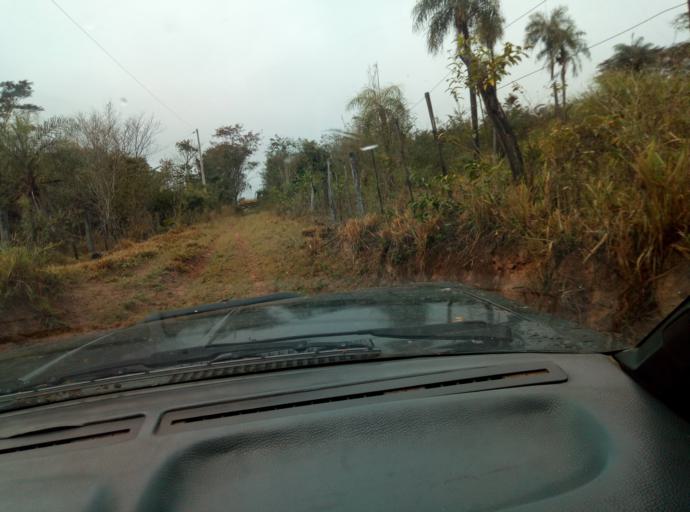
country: PY
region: Caaguazu
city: Carayao
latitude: -25.1973
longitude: -56.3544
